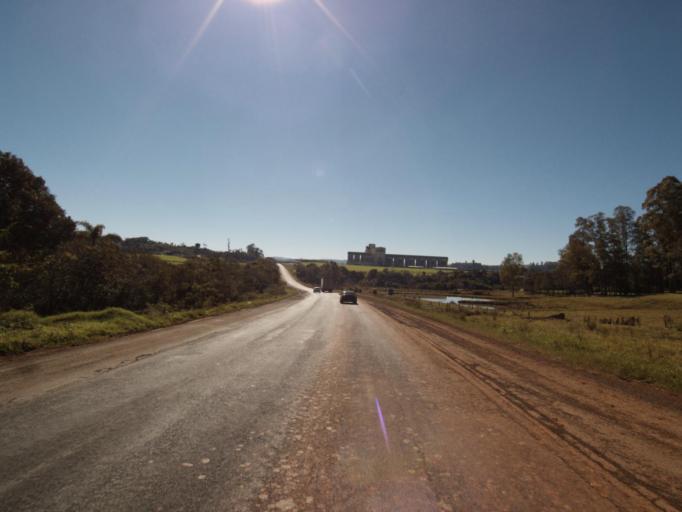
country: BR
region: Rio Grande do Sul
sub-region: Frederico Westphalen
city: Frederico Westphalen
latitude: -26.9134
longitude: -53.1881
